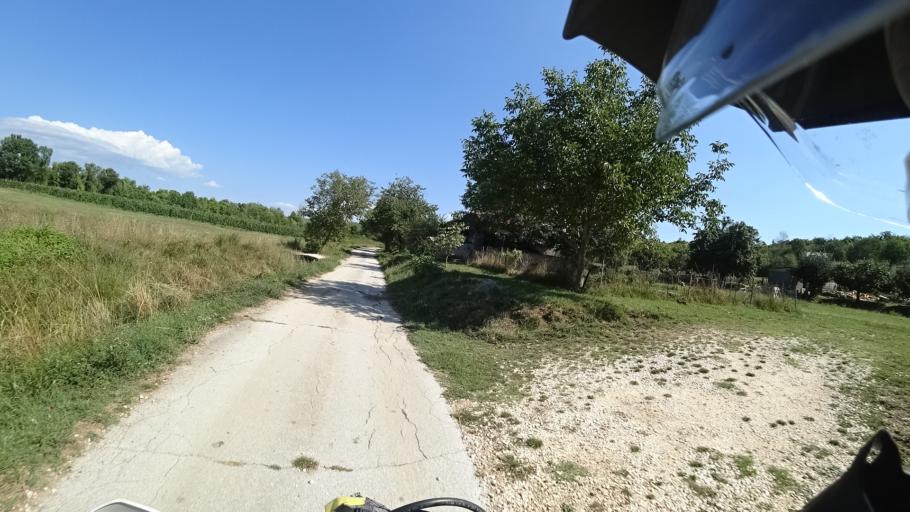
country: HR
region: Sibensko-Kniniska
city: Drnis
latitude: 43.8583
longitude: 16.2293
